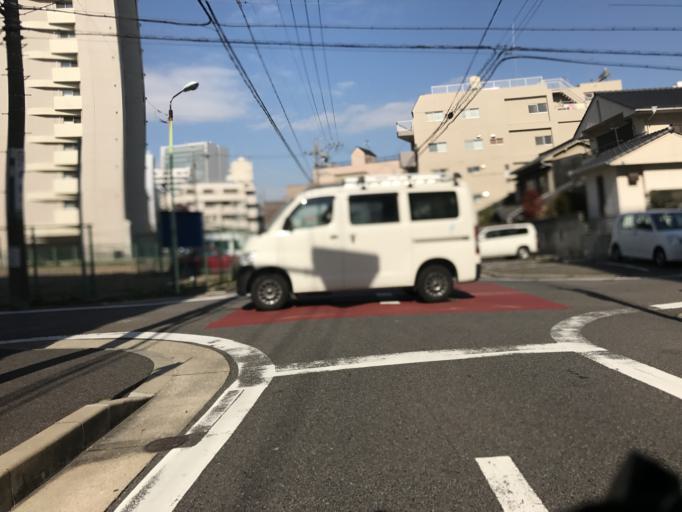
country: JP
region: Aichi
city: Nagoya-shi
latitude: 35.1709
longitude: 136.9350
